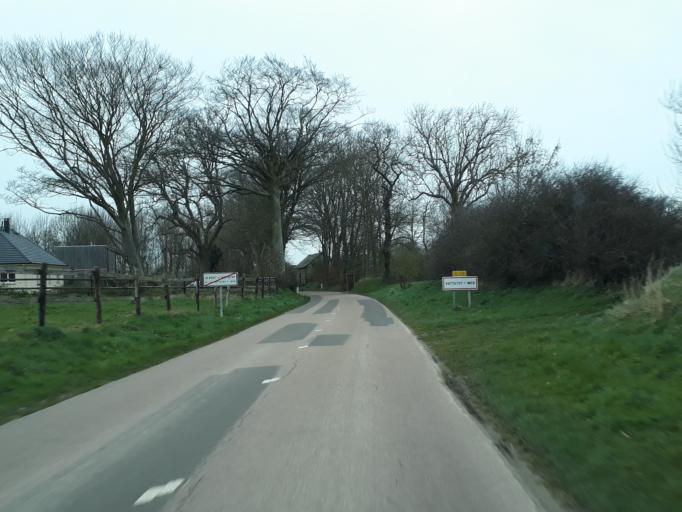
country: FR
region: Haute-Normandie
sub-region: Departement de la Seine-Maritime
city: Les Loges
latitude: 49.7200
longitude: 0.2825
